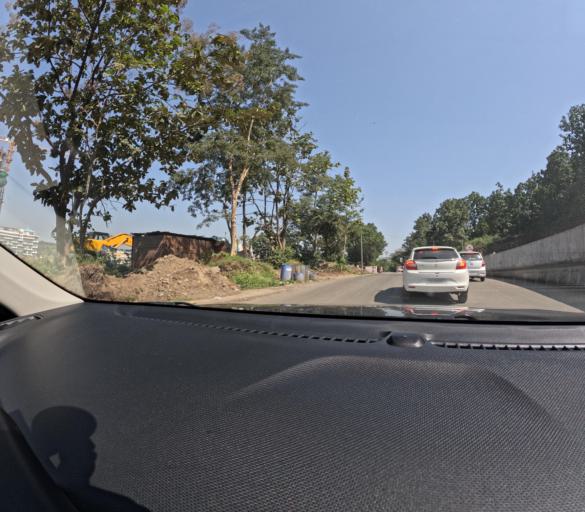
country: IN
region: Maharashtra
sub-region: Pune Division
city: Kharakvasla
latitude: 18.5051
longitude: 73.7861
